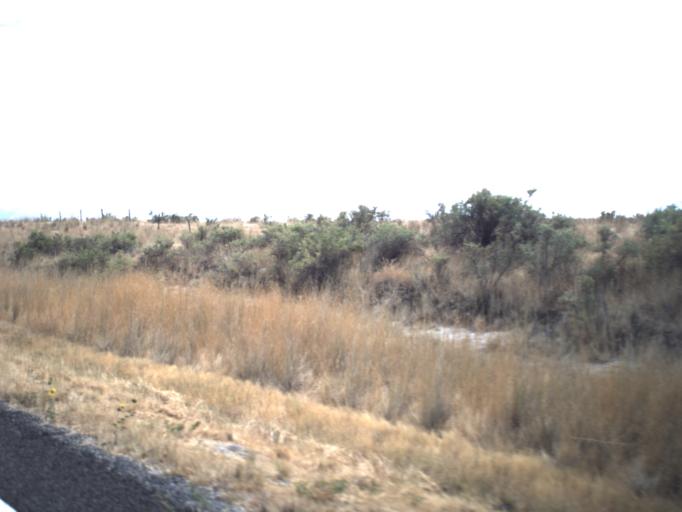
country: US
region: Utah
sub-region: Box Elder County
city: Tremonton
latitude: 41.5873
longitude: -112.2676
